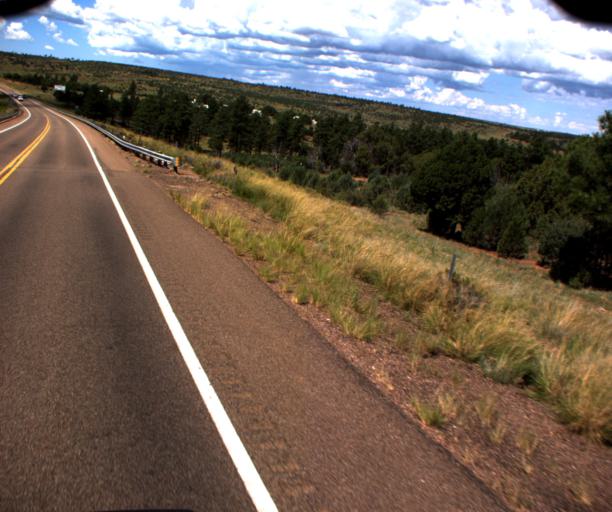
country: US
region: Arizona
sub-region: Navajo County
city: Heber-Overgaard
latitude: 34.3689
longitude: -110.4014
